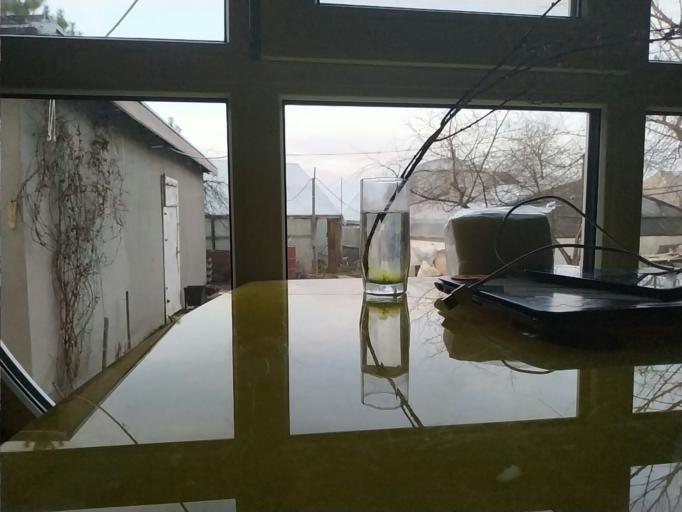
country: RU
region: Republic of Karelia
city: Suoyarvi
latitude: 62.4777
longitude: 31.9914
